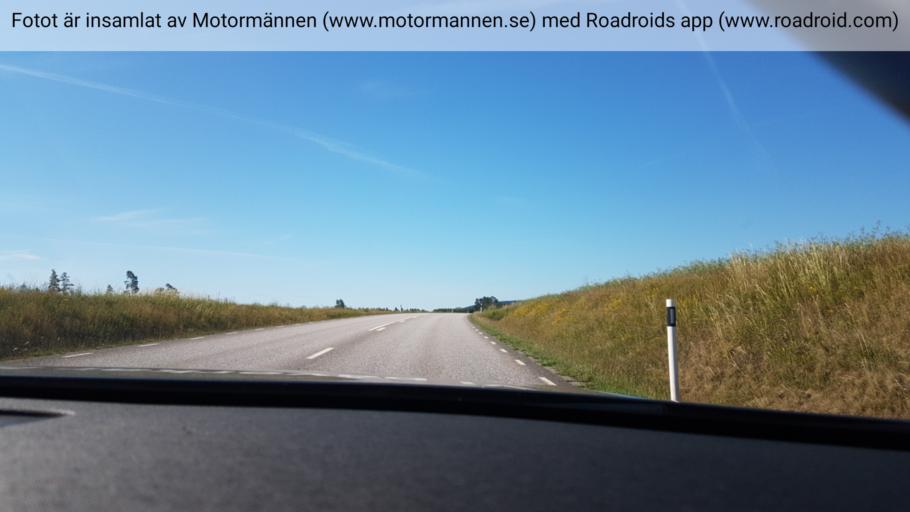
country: SE
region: Vaestra Goetaland
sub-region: Ulricehamns Kommun
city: Ulricehamn
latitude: 57.8758
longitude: 13.4345
